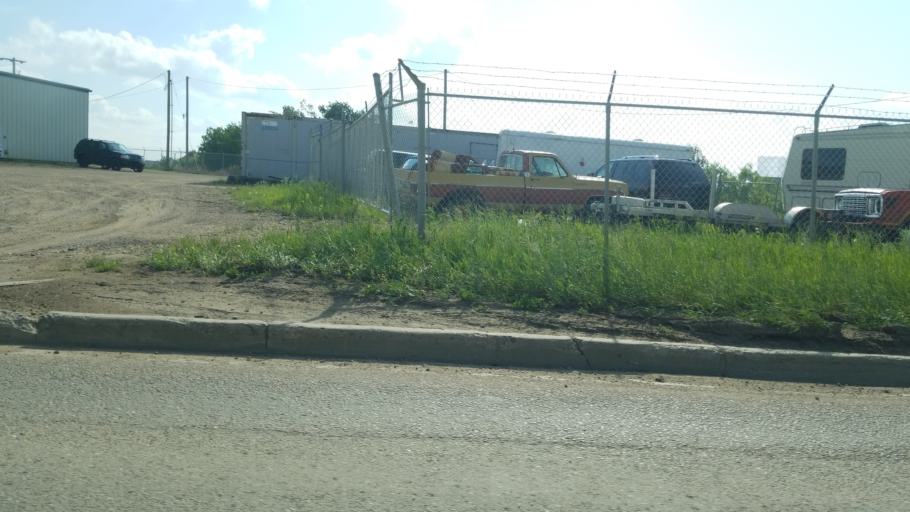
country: CA
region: Saskatchewan
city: Lloydminster
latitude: 53.2844
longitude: -110.0344
